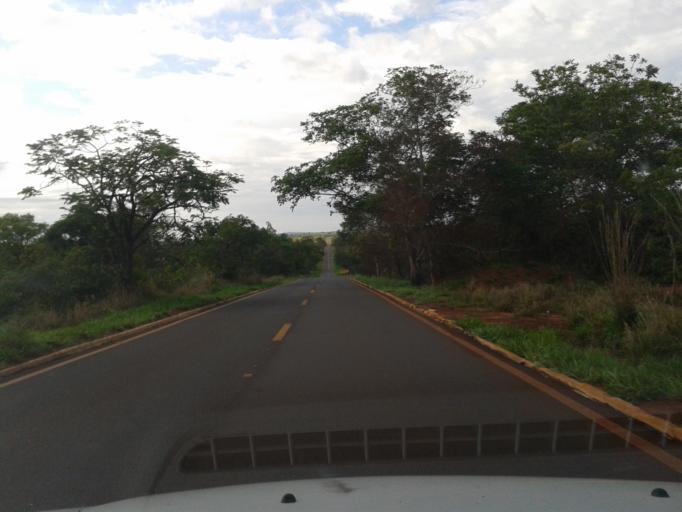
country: BR
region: Minas Gerais
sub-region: Ituiutaba
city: Ituiutaba
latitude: -19.0730
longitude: -49.7661
